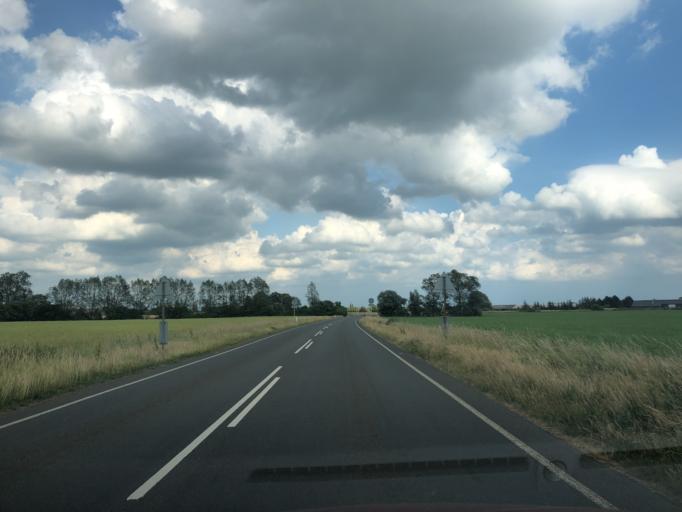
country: DK
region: Zealand
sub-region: Stevns Kommune
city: Harlev
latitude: 55.3151
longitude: 12.2089
